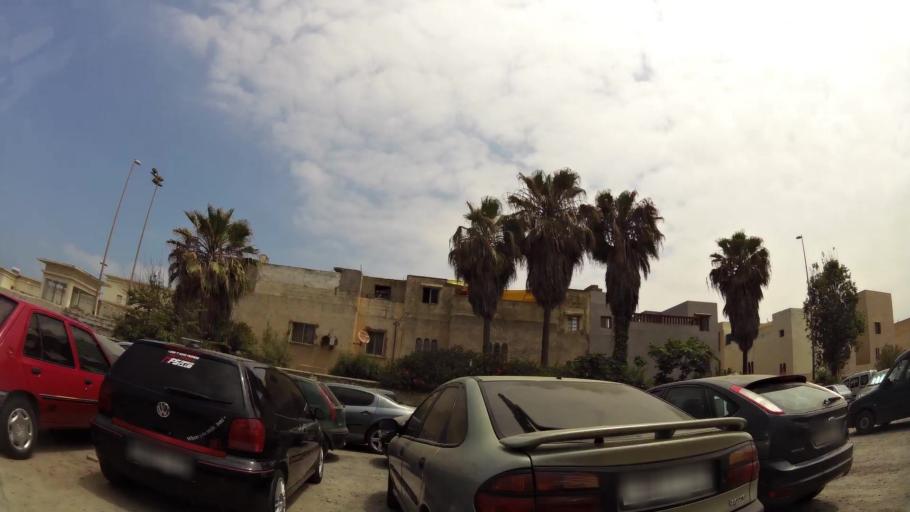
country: MA
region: Rabat-Sale-Zemmour-Zaer
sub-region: Rabat
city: Rabat
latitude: 33.9876
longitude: -6.8868
